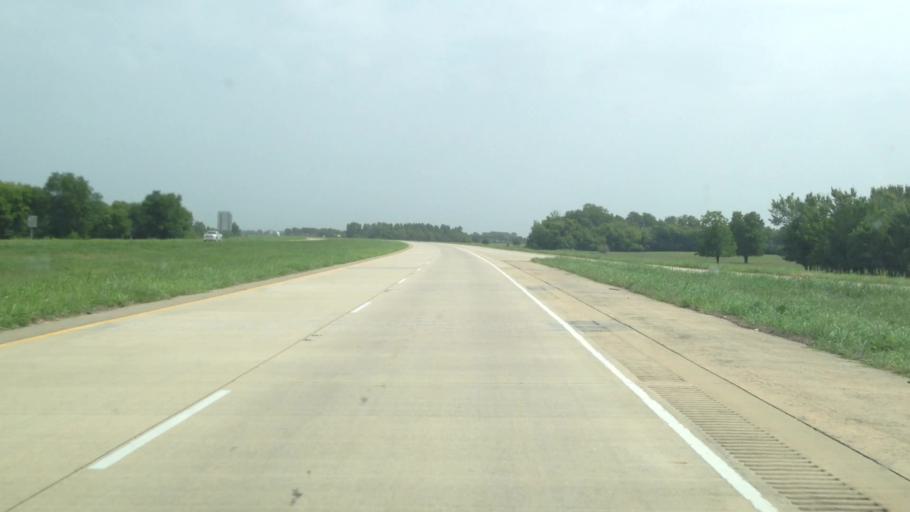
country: US
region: Louisiana
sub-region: Caddo Parish
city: Vivian
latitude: 32.8555
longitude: -93.8625
